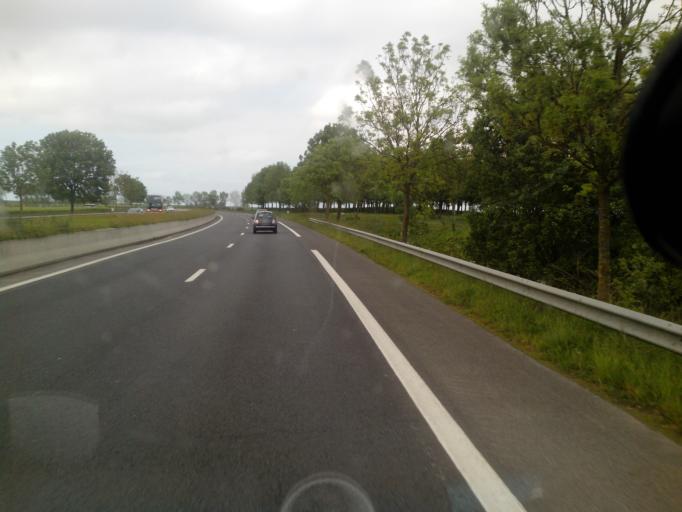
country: FR
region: Lower Normandy
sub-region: Departement du Calvados
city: Mathieu
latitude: 49.2660
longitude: -0.3781
